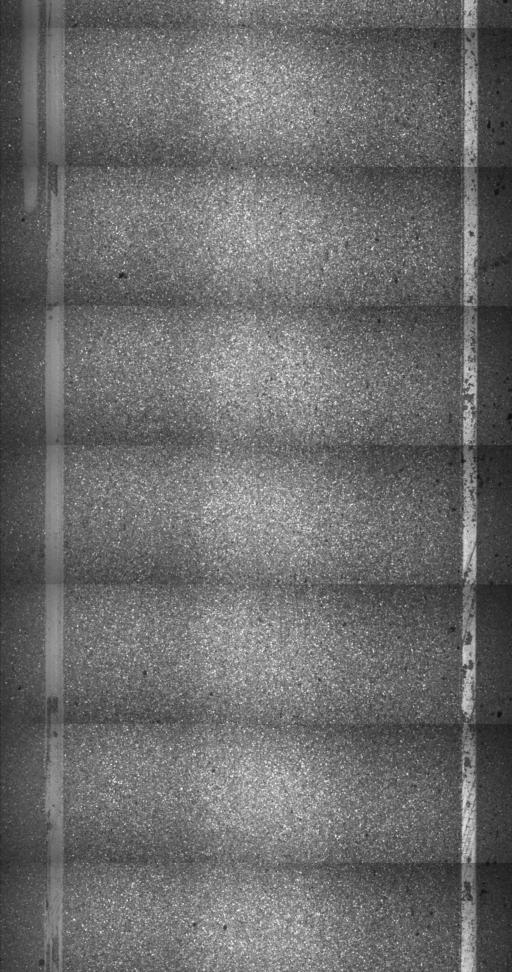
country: US
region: Vermont
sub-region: Addison County
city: Vergennes
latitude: 44.1027
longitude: -73.2961
